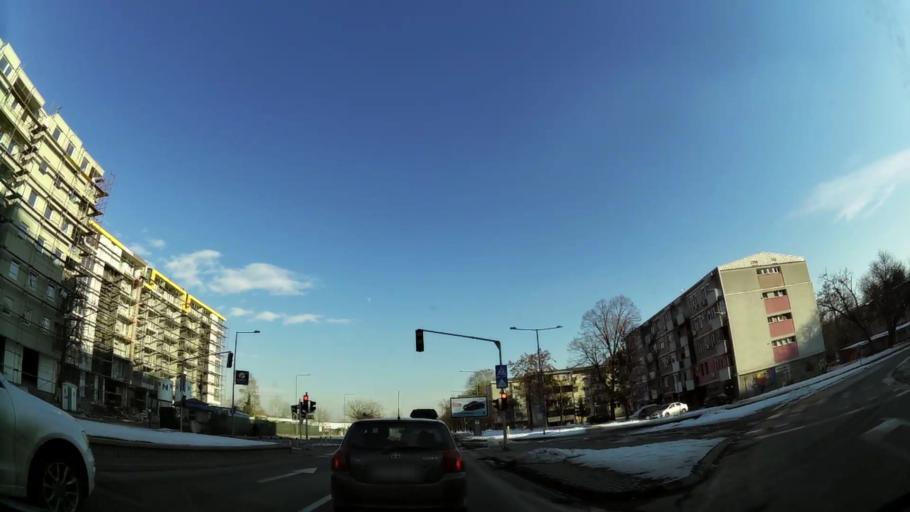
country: MK
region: Karpos
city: Skopje
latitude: 42.0077
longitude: 21.3934
